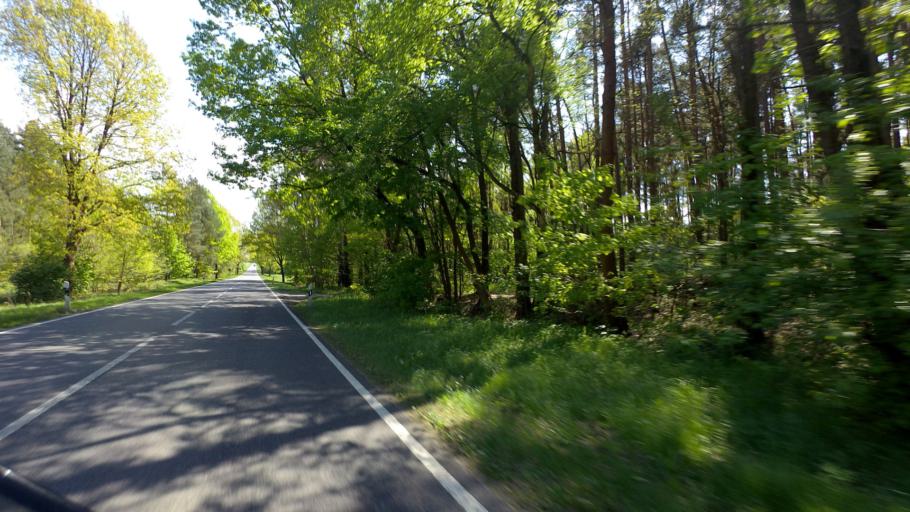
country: DE
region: Brandenburg
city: Lieberose
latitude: 51.9906
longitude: 14.2067
